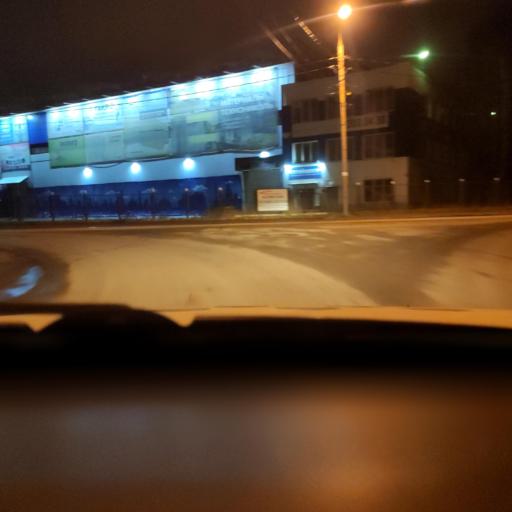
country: RU
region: Perm
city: Perm
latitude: 57.9769
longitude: 56.2670
